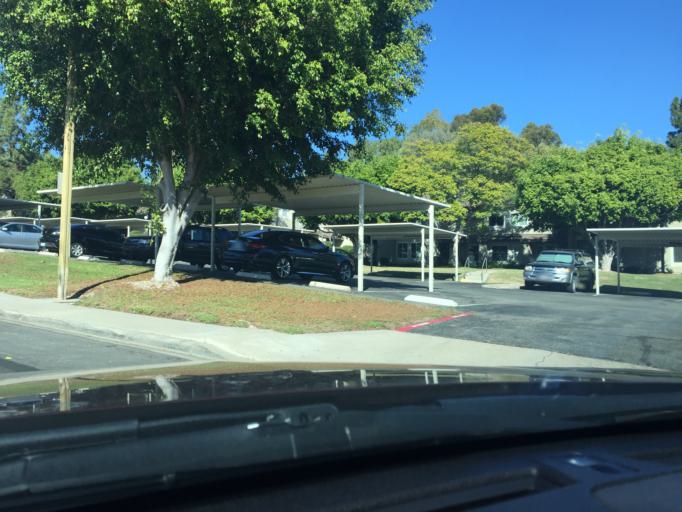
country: US
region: California
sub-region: San Diego County
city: La Mesa
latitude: 32.8222
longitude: -117.0953
